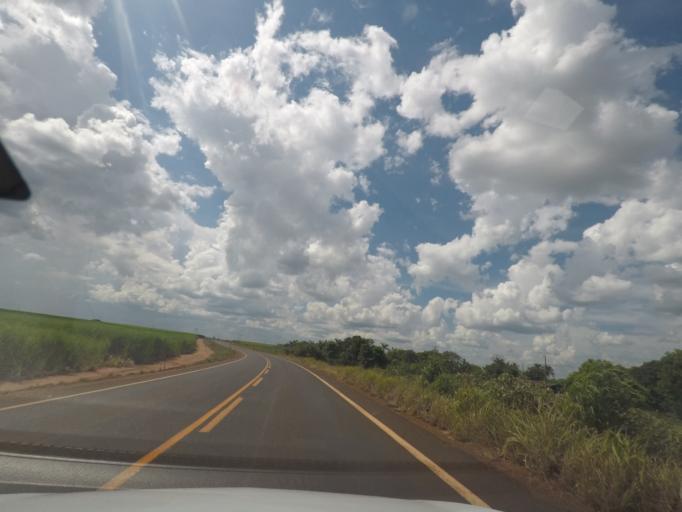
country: BR
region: Minas Gerais
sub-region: Conceicao Das Alagoas
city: Conceicao das Alagoas
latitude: -19.8335
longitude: -48.5899
